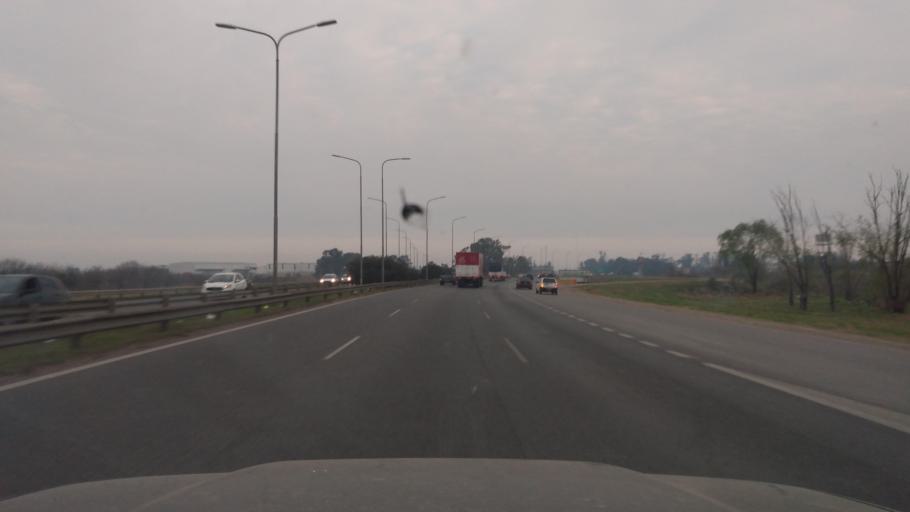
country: AR
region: Buenos Aires
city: Hurlingham
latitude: -34.5191
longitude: -58.5911
